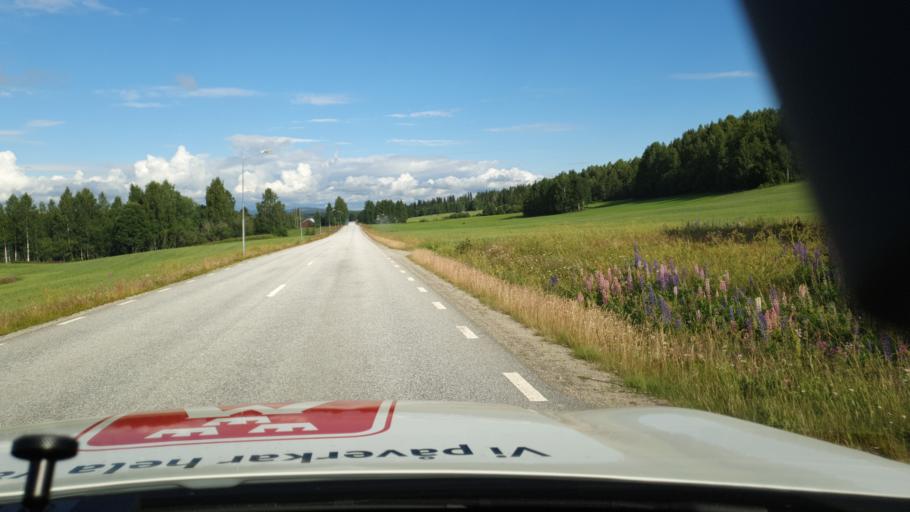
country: SE
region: Vaesterbotten
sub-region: Vindelns Kommun
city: Vindeln
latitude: 64.1700
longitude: 19.4905
